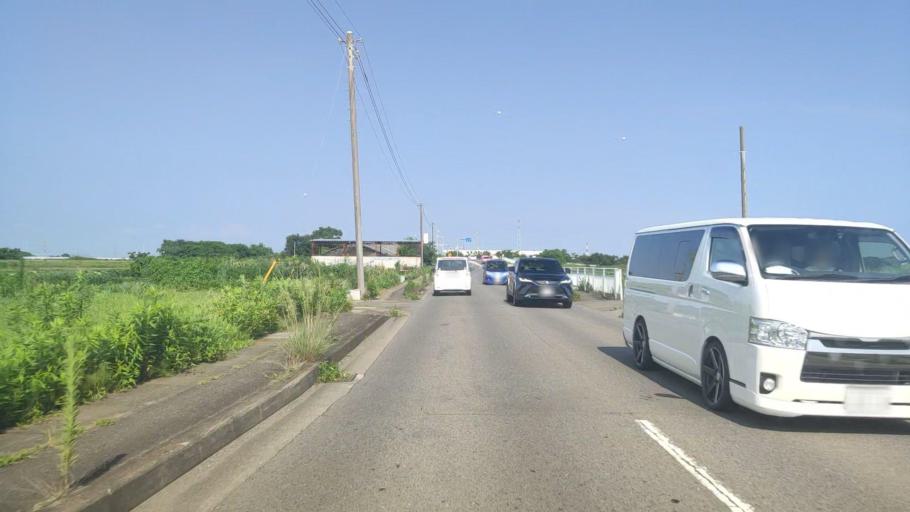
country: JP
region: Kanagawa
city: Isehara
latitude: 35.3650
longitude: 139.3176
